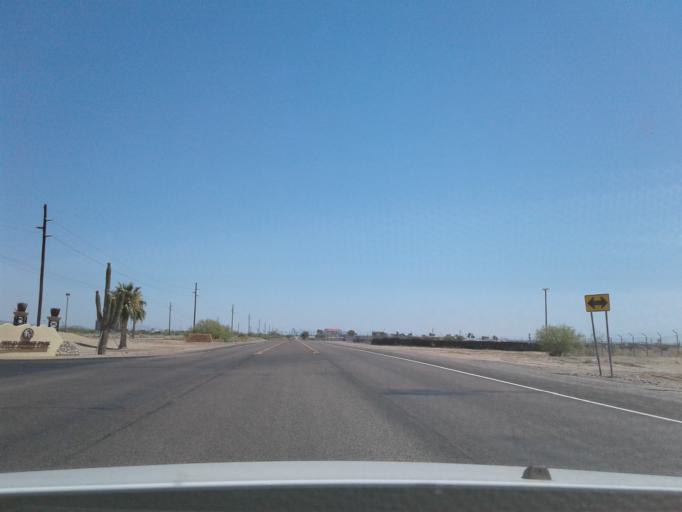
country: US
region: Arizona
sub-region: Maricopa County
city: Guadalupe
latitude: 33.2621
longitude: -111.9745
